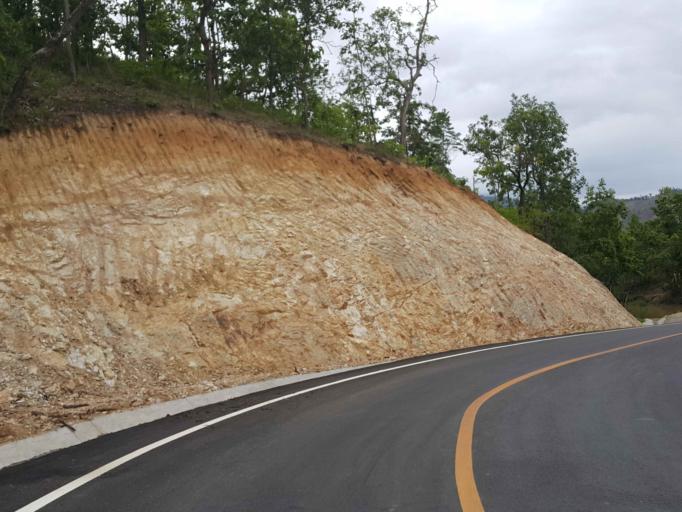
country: TH
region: Chiang Mai
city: Mae Chaem
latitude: 18.5086
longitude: 98.4119
